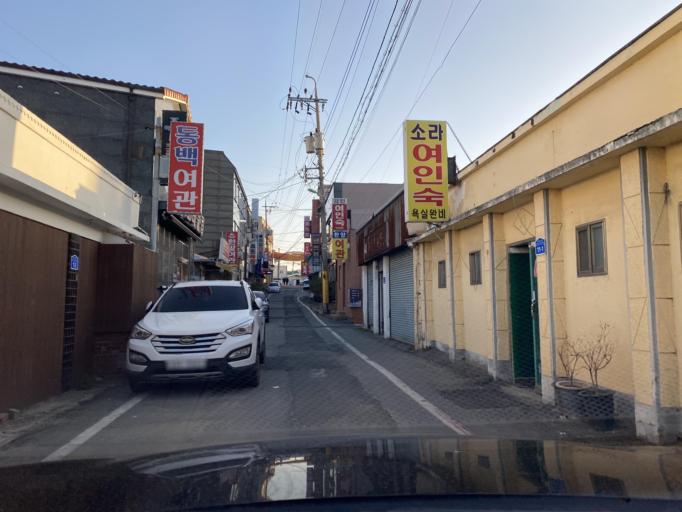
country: KR
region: Chungcheongnam-do
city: Yesan
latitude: 36.6872
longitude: 126.8306
